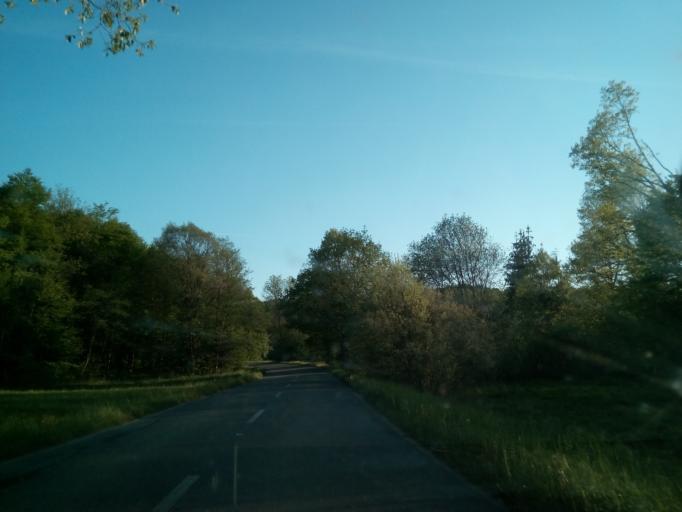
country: CZ
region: South Moravian
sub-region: Okres Blansko
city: Jedovnice
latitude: 49.3291
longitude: 16.7404
